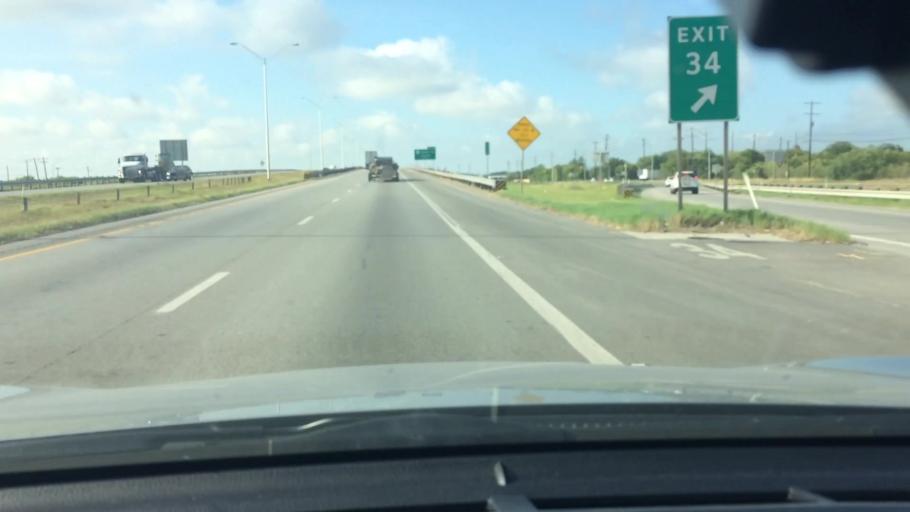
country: US
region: Texas
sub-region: Bexar County
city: Kirby
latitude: 29.4262
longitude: -98.3894
